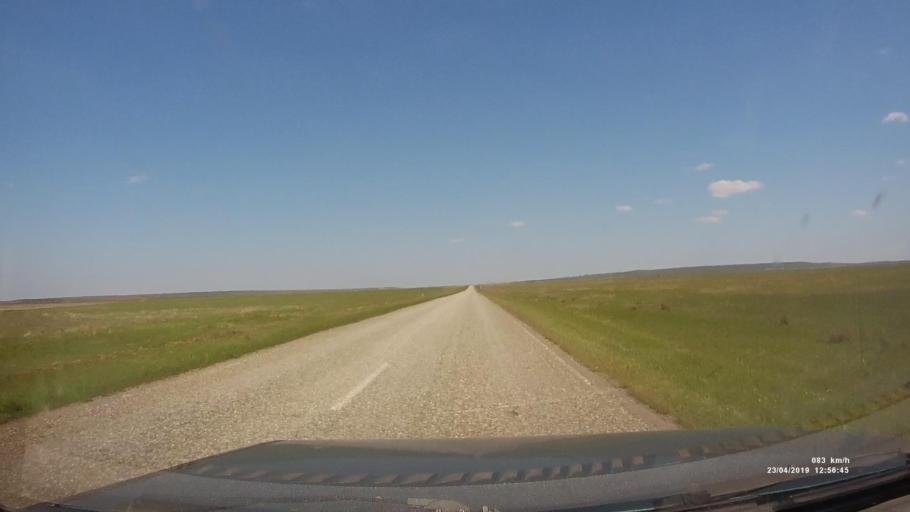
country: RU
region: Kalmykiya
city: Yashalta
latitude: 46.5972
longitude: 42.5746
